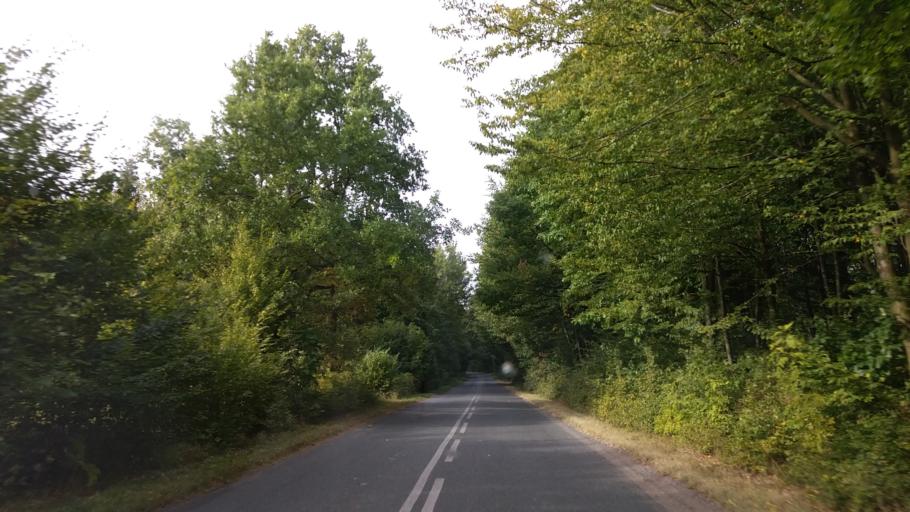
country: PL
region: West Pomeranian Voivodeship
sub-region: Powiat choszczenski
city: Krzecin
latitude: 53.0241
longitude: 15.5110
